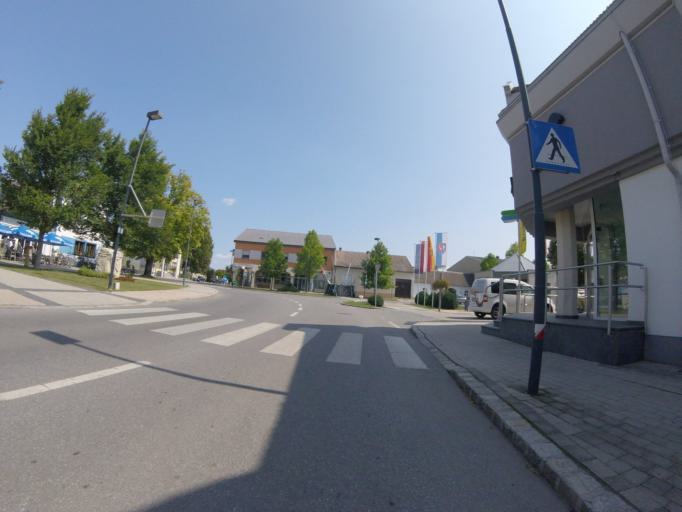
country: AT
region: Burgenland
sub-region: Politischer Bezirk Neusiedl am See
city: Illmitz
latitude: 47.7619
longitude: 16.7993
